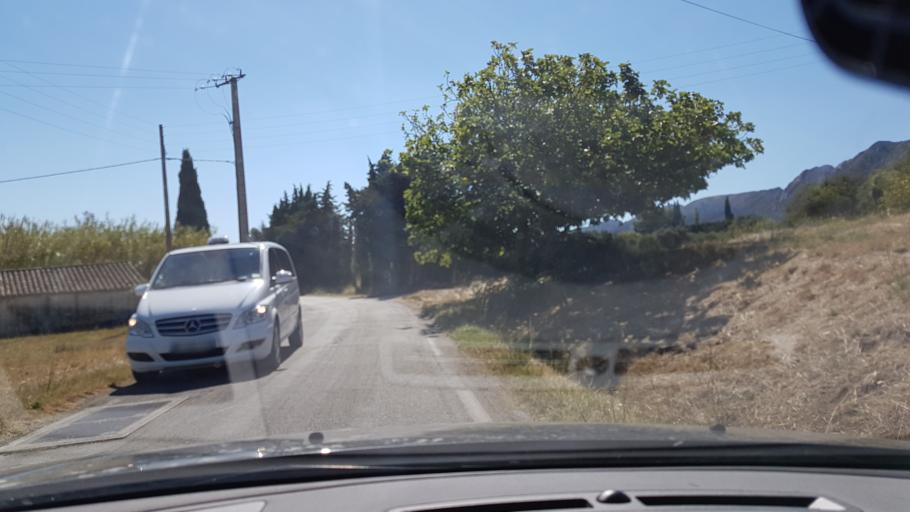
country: FR
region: Provence-Alpes-Cote d'Azur
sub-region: Departement des Bouches-du-Rhone
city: Eygalieres
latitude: 43.7638
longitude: 4.9311
